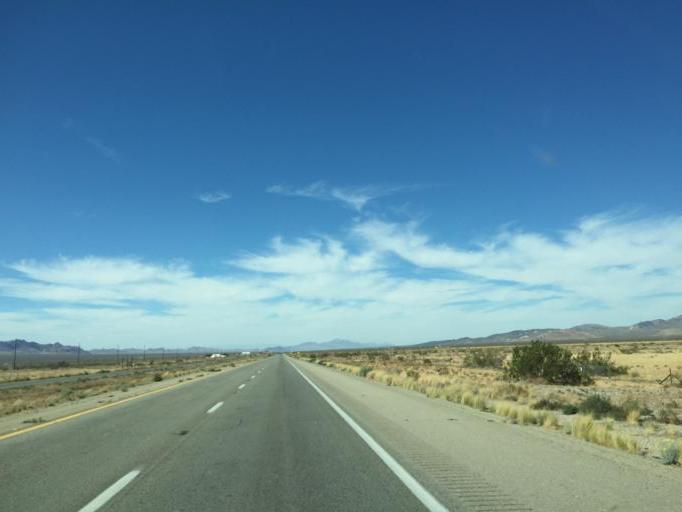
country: US
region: Arizona
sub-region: Mohave County
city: Dolan Springs
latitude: 35.5412
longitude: -114.3602
